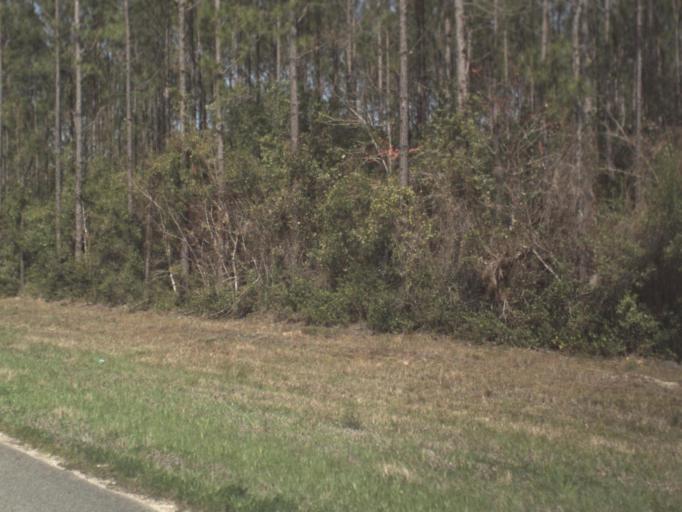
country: US
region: Florida
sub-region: Liberty County
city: Bristol
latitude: 30.3860
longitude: -84.7628
